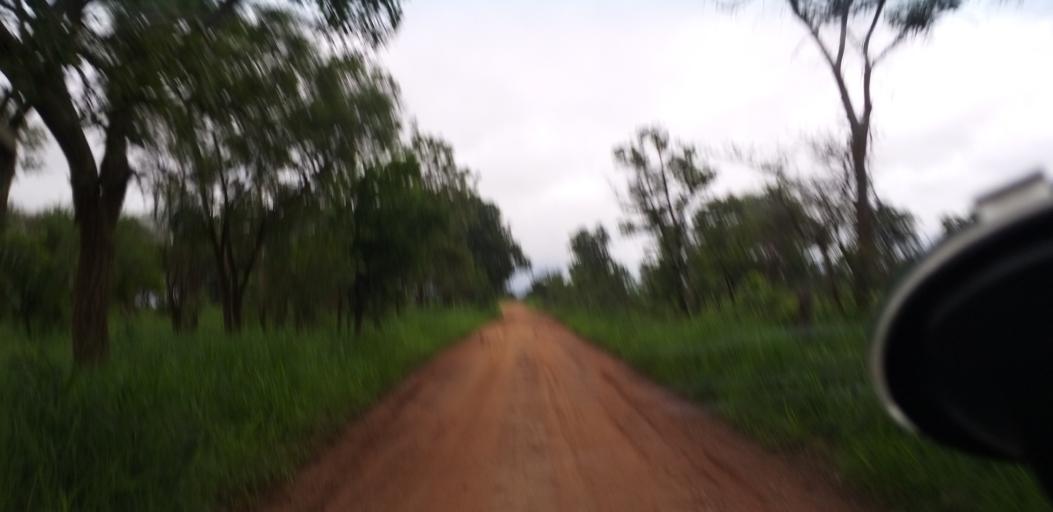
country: ZM
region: Lusaka
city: Lusaka
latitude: -15.5276
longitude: 28.3101
